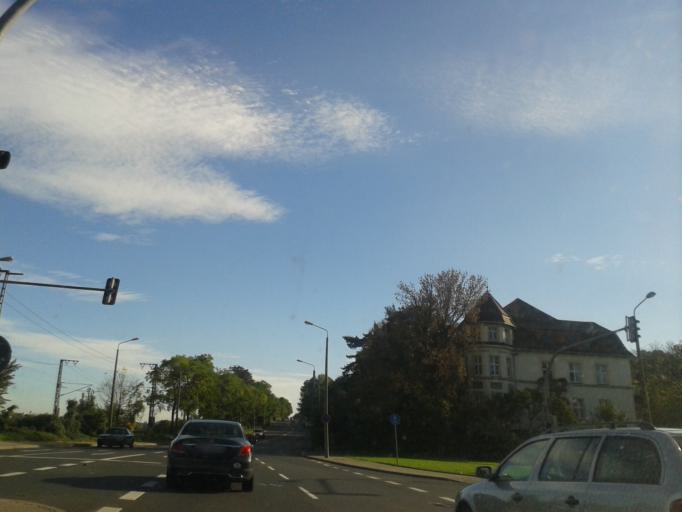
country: DE
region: Saxony
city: Radebeul
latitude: 51.0715
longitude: 13.6707
